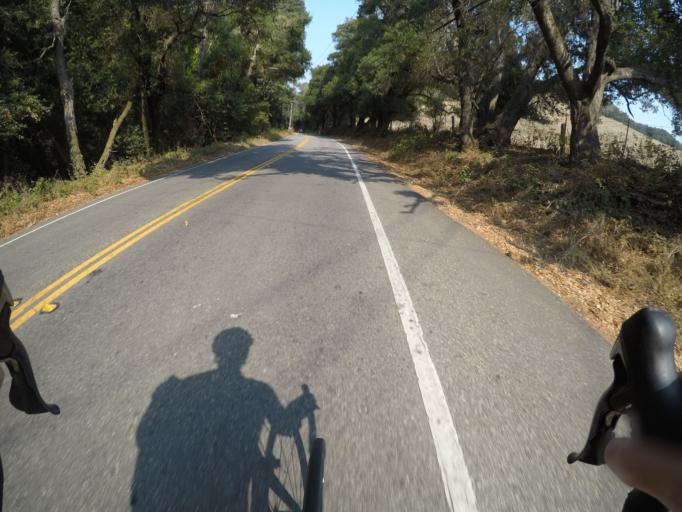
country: US
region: California
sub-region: Santa Cruz County
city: Pasatiempo
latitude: 36.9996
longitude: -122.0094
